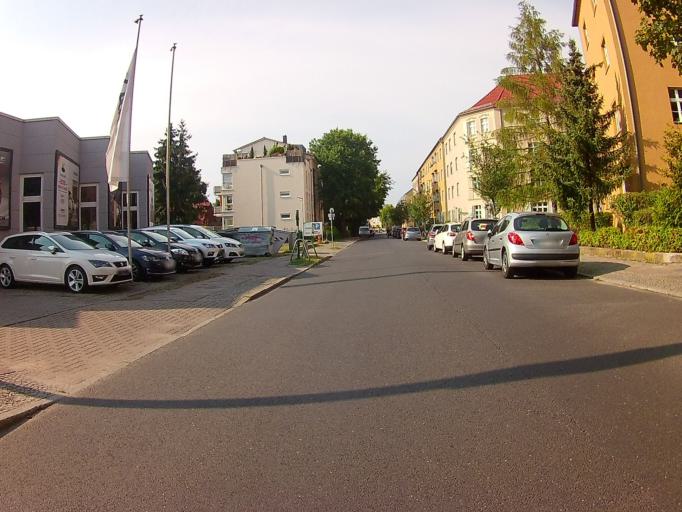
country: DE
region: Berlin
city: Kopenick Bezirk
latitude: 52.4546
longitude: 13.5742
